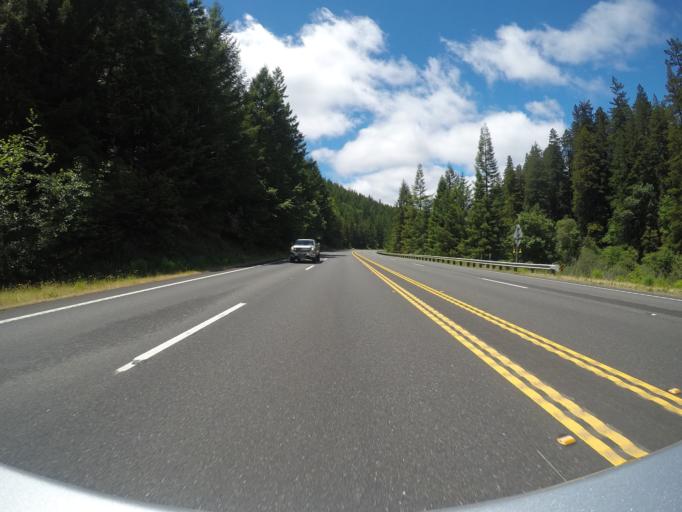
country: US
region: California
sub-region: Humboldt County
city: Redway
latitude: 40.2585
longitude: -123.8421
